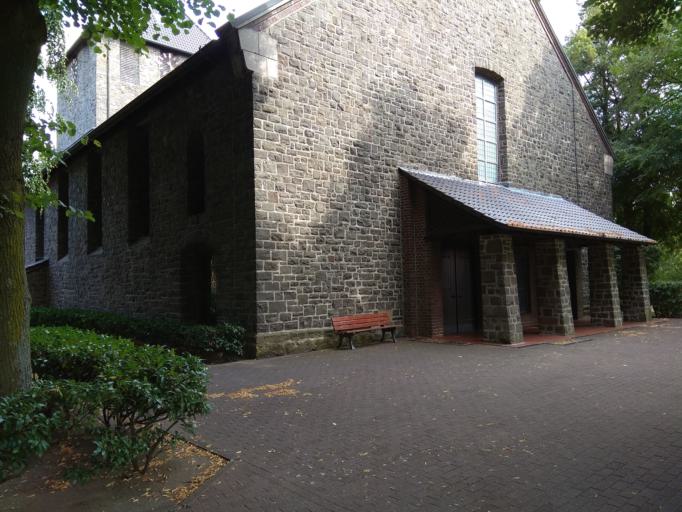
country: DE
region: North Rhine-Westphalia
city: Marl
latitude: 51.7141
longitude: 7.0959
